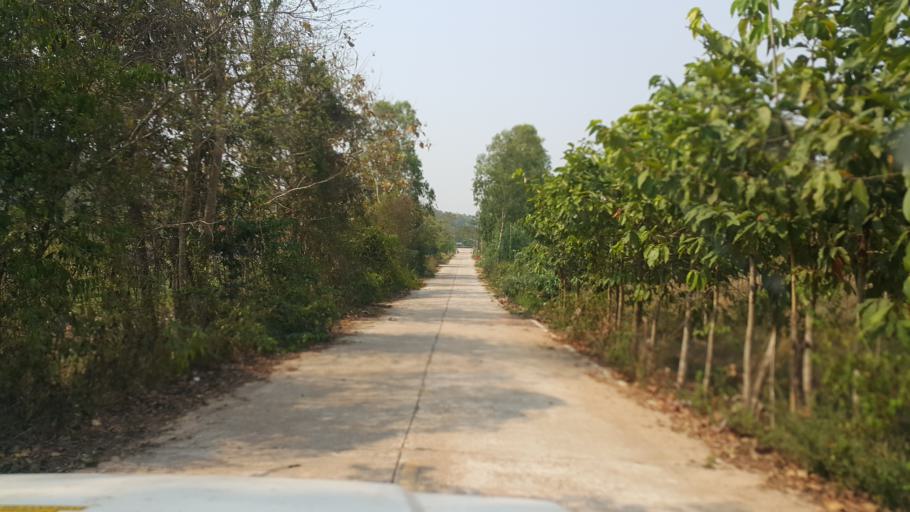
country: TH
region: Nakhon Phanom
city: Ban Phaeng
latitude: 17.9837
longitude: 104.1459
